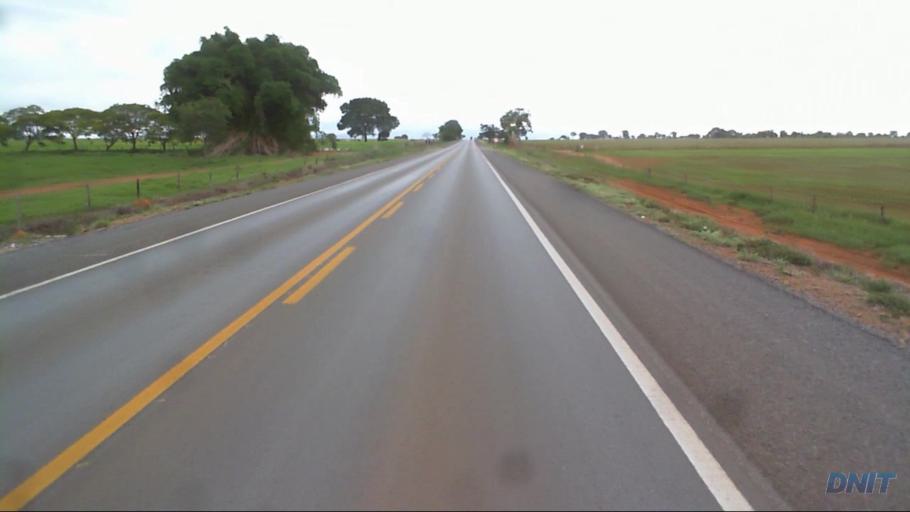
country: BR
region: Goias
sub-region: Padre Bernardo
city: Padre Bernardo
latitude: -15.2184
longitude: -48.6213
